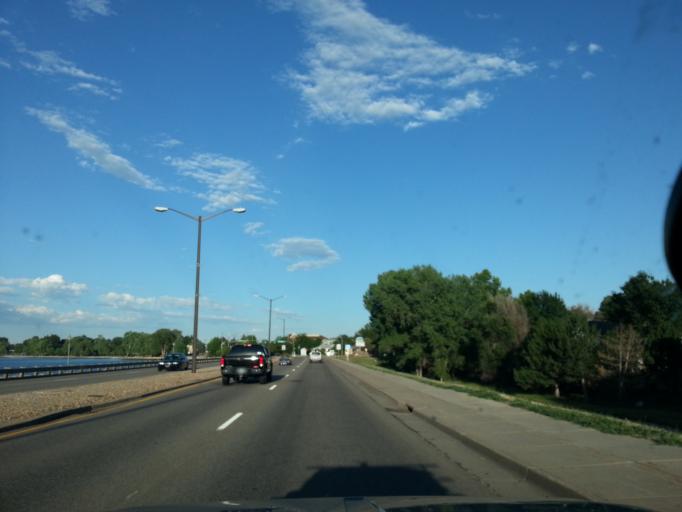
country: US
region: Colorado
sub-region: Larimer County
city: Loveland
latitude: 40.4050
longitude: -105.0903
